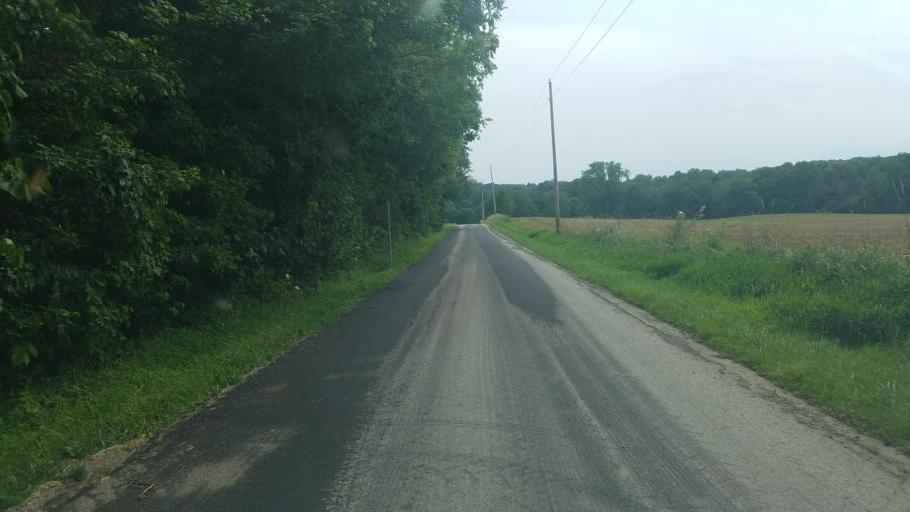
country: US
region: Ohio
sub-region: Richland County
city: Lexington
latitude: 40.6659
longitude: -82.6391
